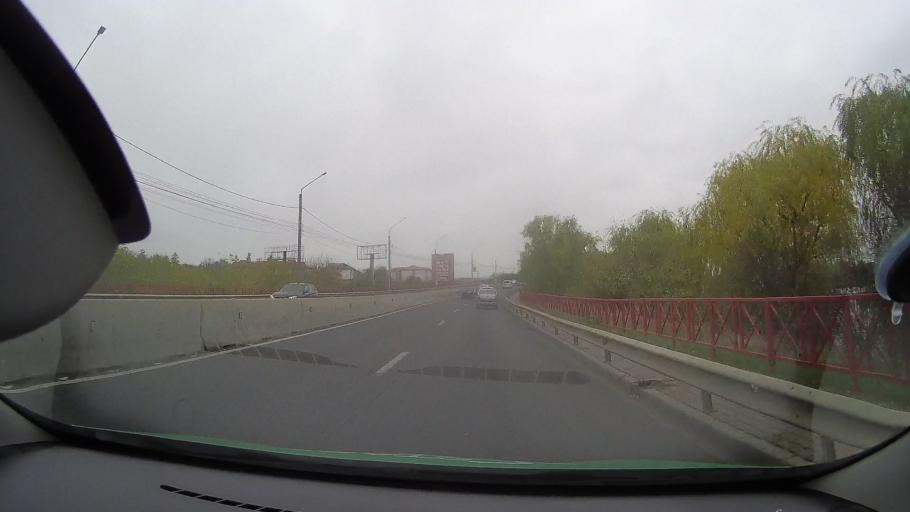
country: RO
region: Ilfov
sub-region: Comuna Corbeanca
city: Corbeanca
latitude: 44.6131
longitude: 26.0713
